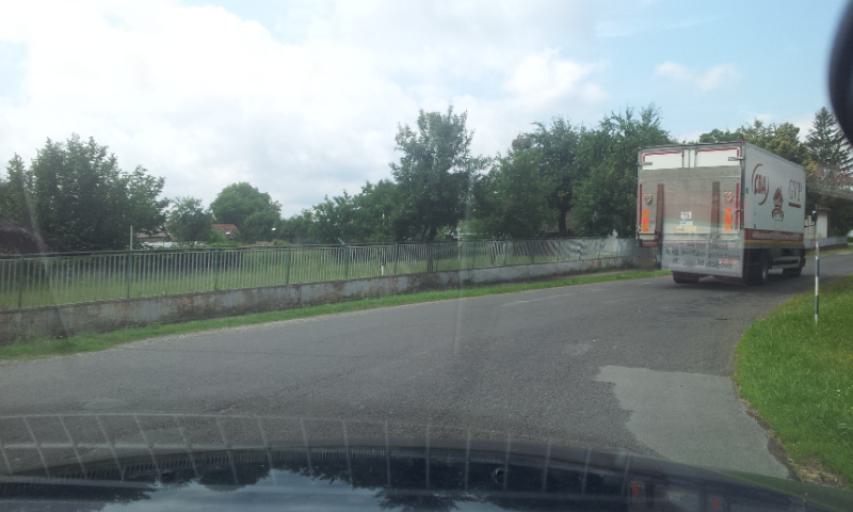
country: SK
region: Kosicky
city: Michalovce
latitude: 48.6242
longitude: 21.9888
